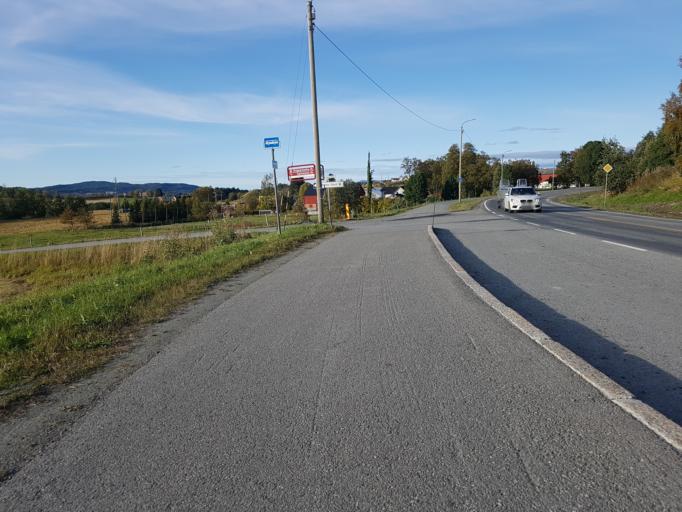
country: NO
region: Sor-Trondelag
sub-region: Trondheim
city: Trondheim
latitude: 63.3741
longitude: 10.4300
